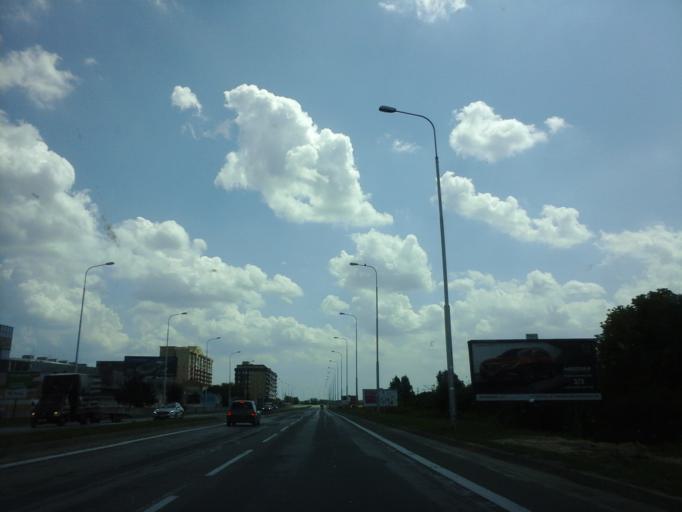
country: AT
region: Burgenland
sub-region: Politischer Bezirk Neusiedl am See
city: Kittsee
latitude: 48.1011
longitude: 17.0978
